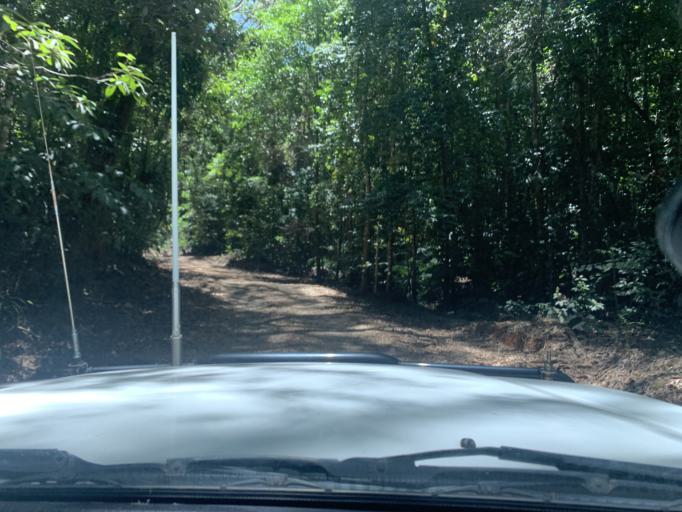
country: AU
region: Queensland
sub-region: Cairns
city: Redlynch
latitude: -16.9417
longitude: 145.6278
